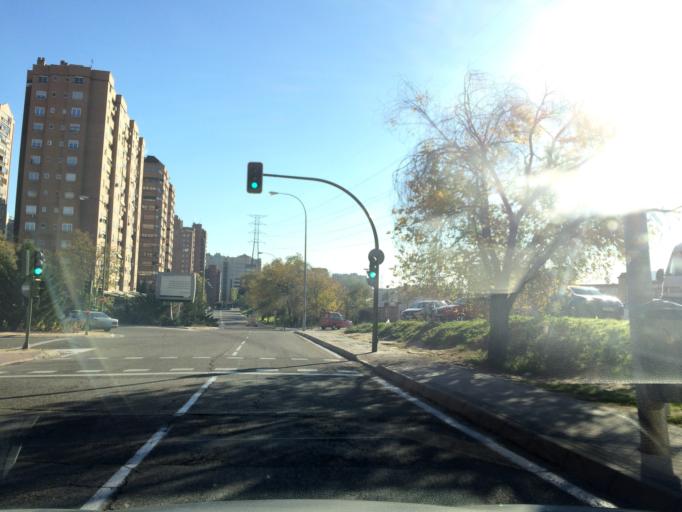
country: ES
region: Madrid
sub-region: Provincia de Madrid
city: Pinar de Chamartin
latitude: 40.4812
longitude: -3.6758
